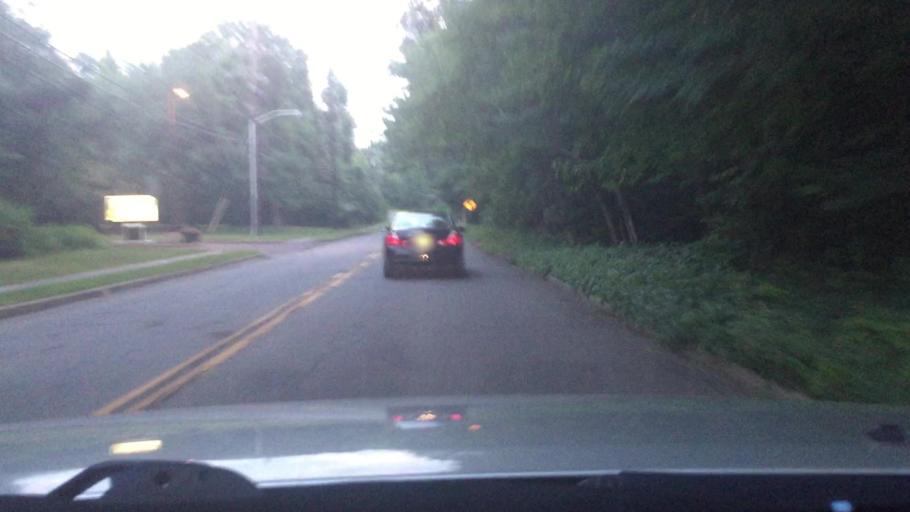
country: US
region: New Jersey
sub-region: Middlesex County
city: Milltown
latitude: 40.4278
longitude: -74.4457
